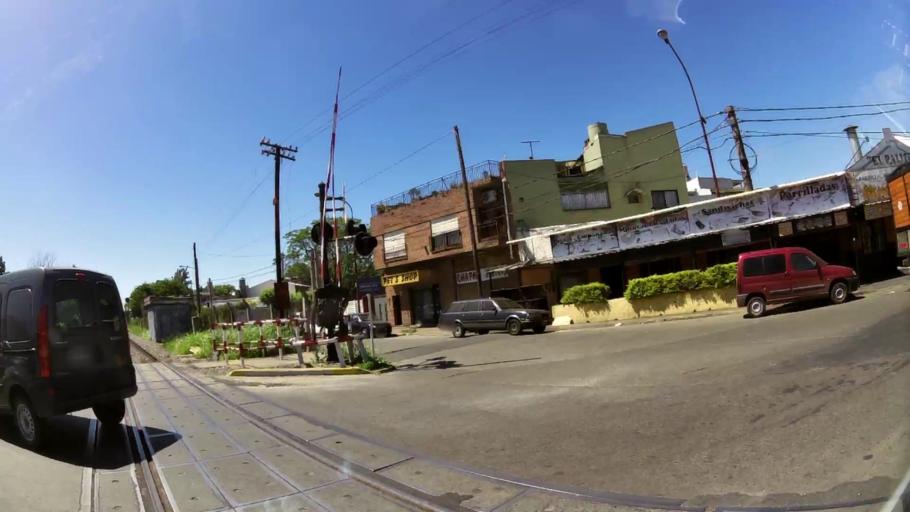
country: AR
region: Buenos Aires
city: Caseros
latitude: -34.5951
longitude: -58.5387
